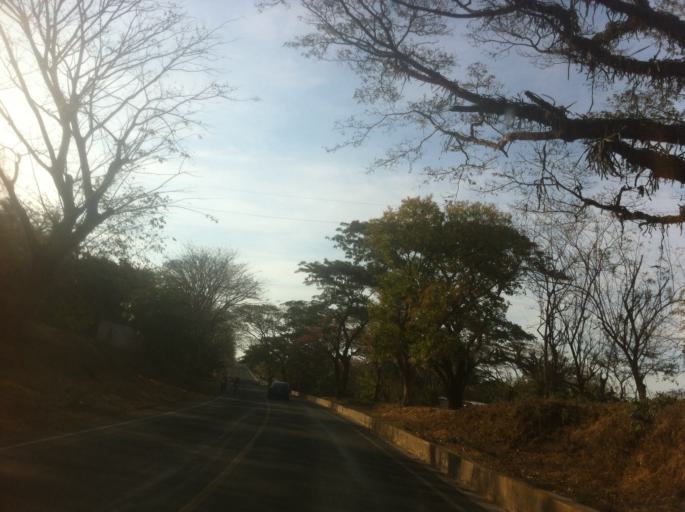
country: NI
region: Rivas
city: Cardenas
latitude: 11.2511
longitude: -85.6308
